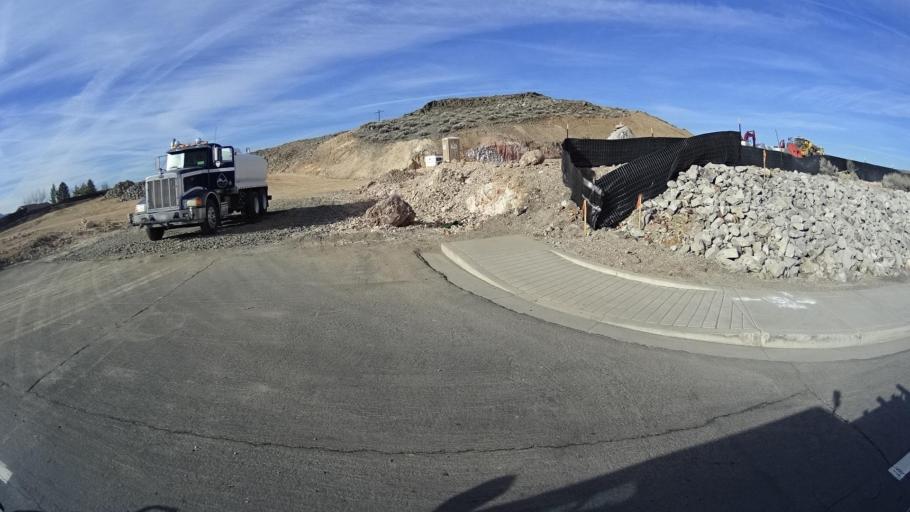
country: US
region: Nevada
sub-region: Washoe County
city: Sparks
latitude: 39.5712
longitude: -119.7206
